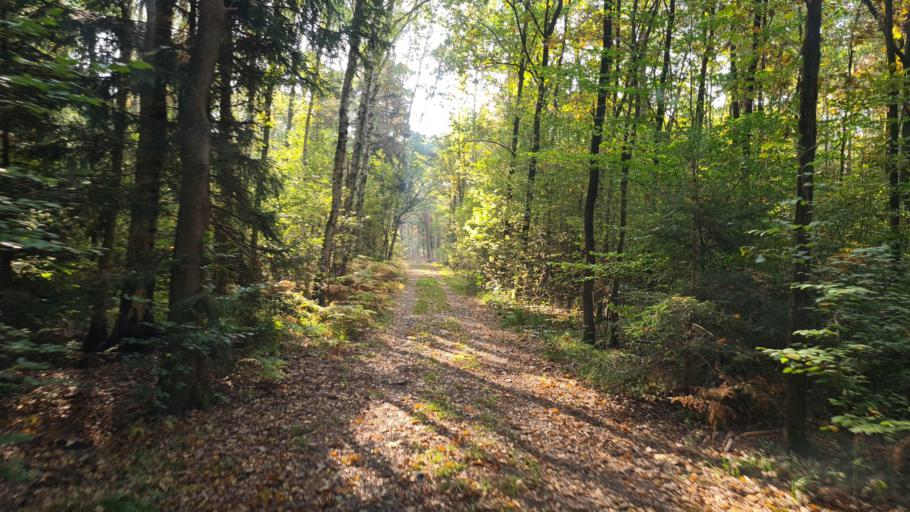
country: DE
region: Brandenburg
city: Schonborn
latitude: 51.6240
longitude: 13.5192
